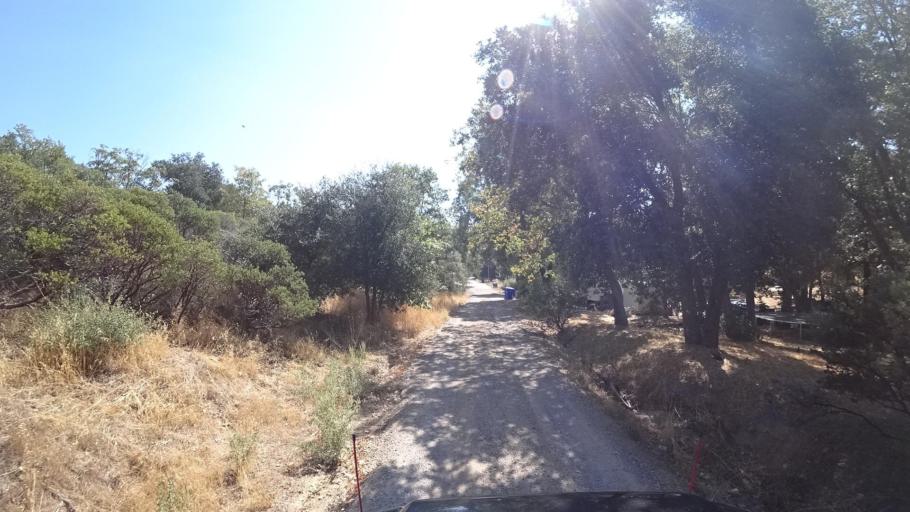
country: US
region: California
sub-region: San Diego County
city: Julian
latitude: 33.0653
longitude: -116.5777
